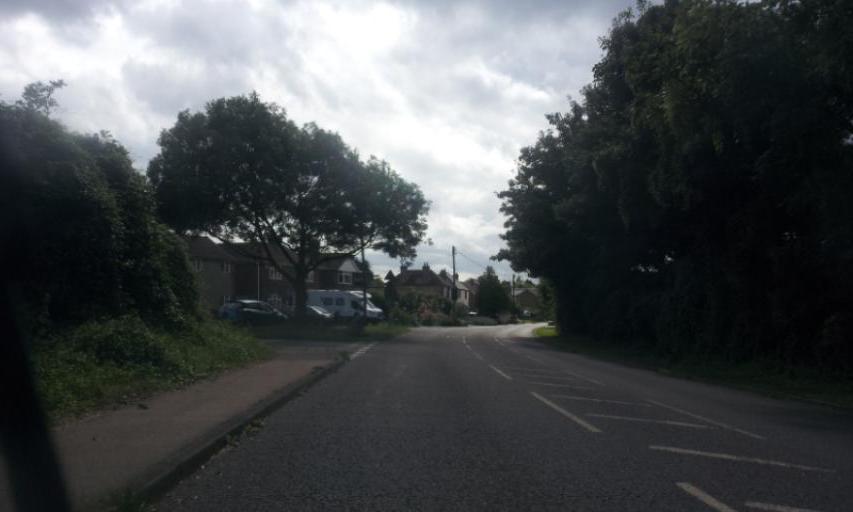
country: GB
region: England
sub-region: Kent
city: Sittingbourne
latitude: 51.3154
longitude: 0.6985
